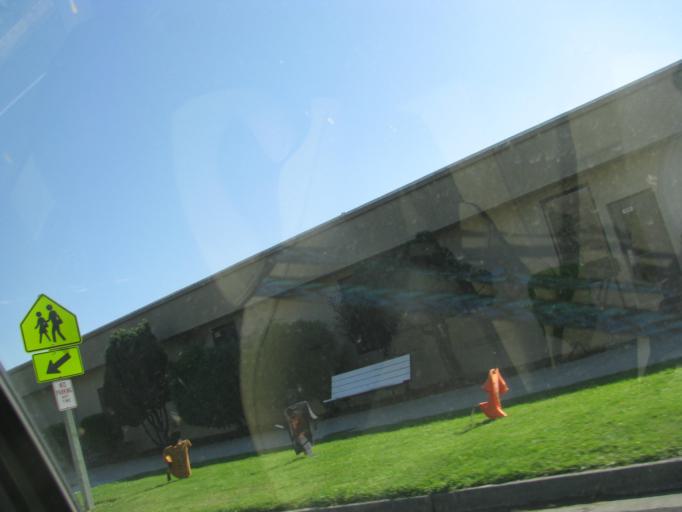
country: US
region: Washington
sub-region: Asotin County
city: Asotin
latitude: 46.3408
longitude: -117.0504
